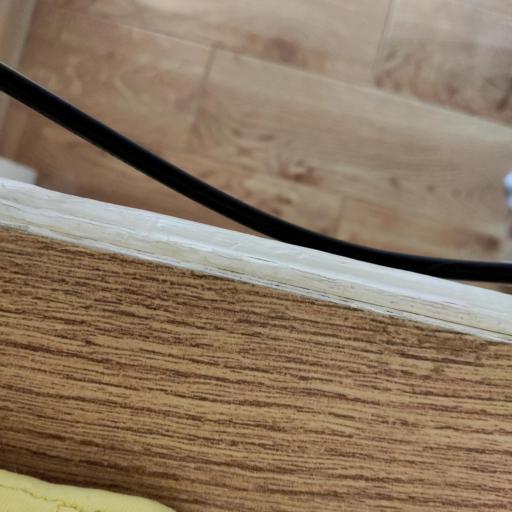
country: RU
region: Moscow
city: Metrogorodok
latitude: 55.8349
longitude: 37.7872
